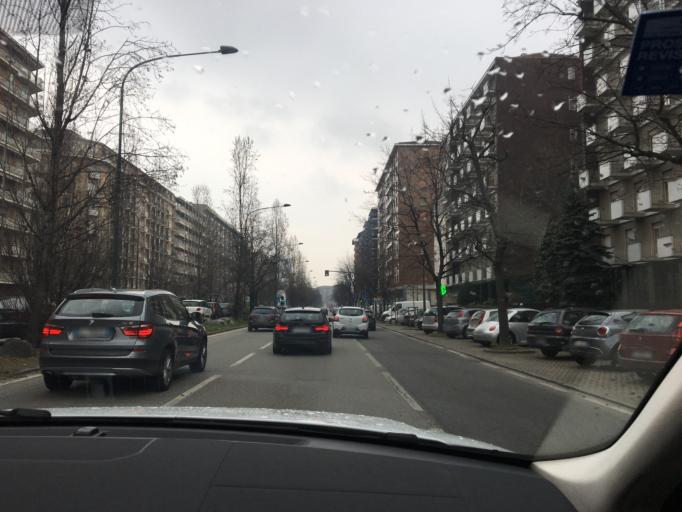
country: IT
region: Piedmont
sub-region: Provincia di Torino
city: Lesna
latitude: 45.0366
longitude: 7.6396
